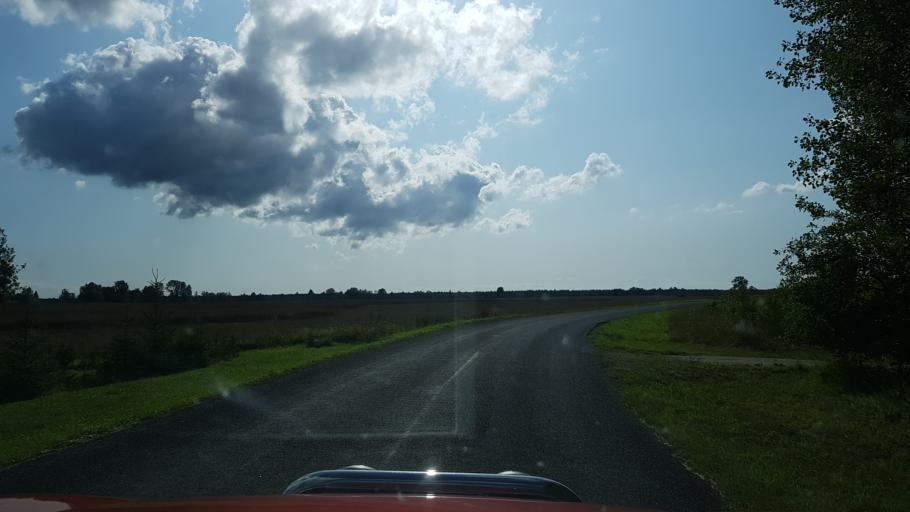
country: EE
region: Harju
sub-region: Paldiski linn
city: Paldiski
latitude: 59.1996
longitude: 23.9630
